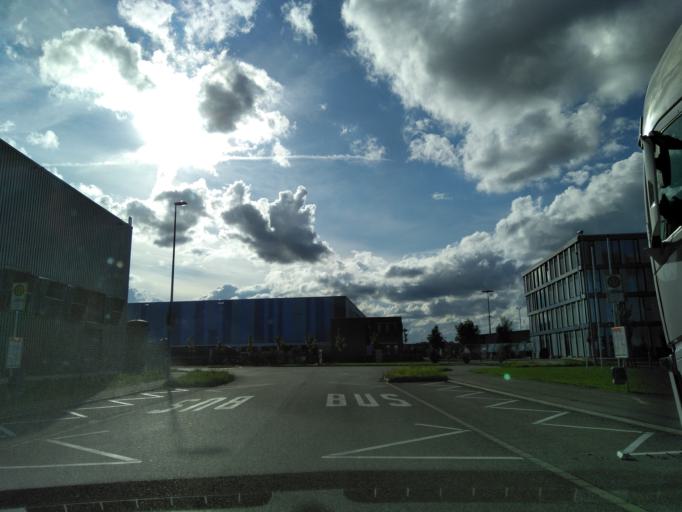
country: DE
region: Baden-Wuerttemberg
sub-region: Regierungsbezirk Stuttgart
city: Oberriexingen
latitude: 48.9519
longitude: 9.0494
